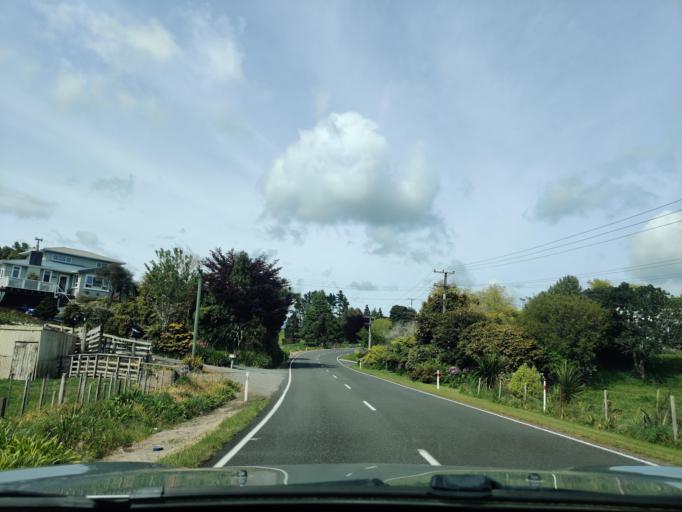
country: NZ
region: Taranaki
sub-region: New Plymouth District
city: New Plymouth
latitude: -39.0953
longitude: 174.1029
